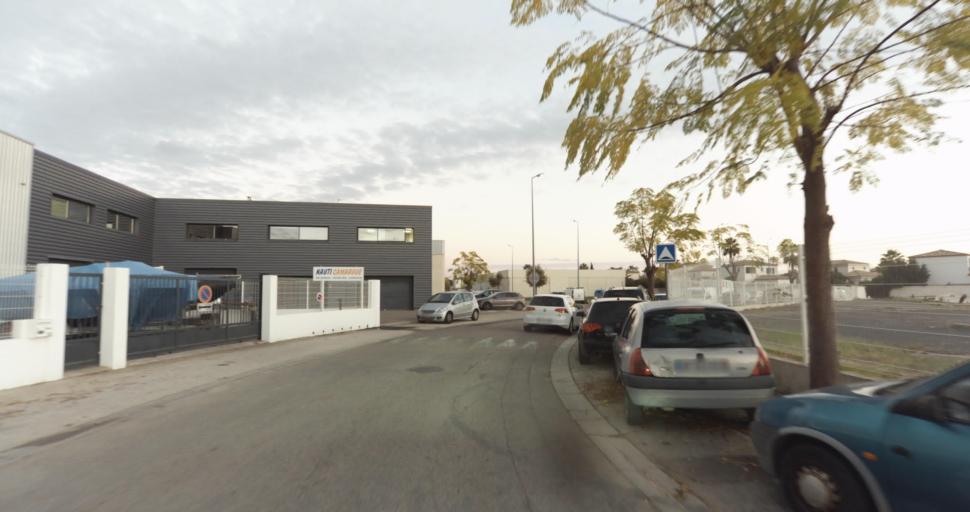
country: FR
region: Languedoc-Roussillon
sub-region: Departement du Gard
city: Aigues-Mortes
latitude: 43.5776
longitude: 4.1885
